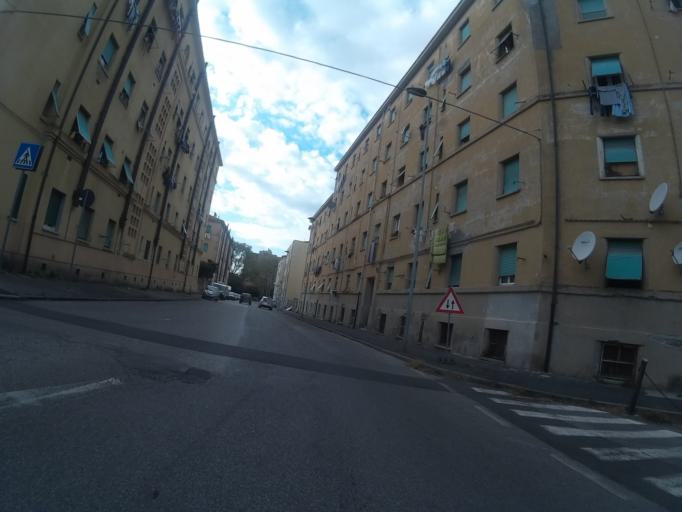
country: IT
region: Tuscany
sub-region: Provincia di Livorno
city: Livorno
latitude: 43.5594
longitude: 10.3239
